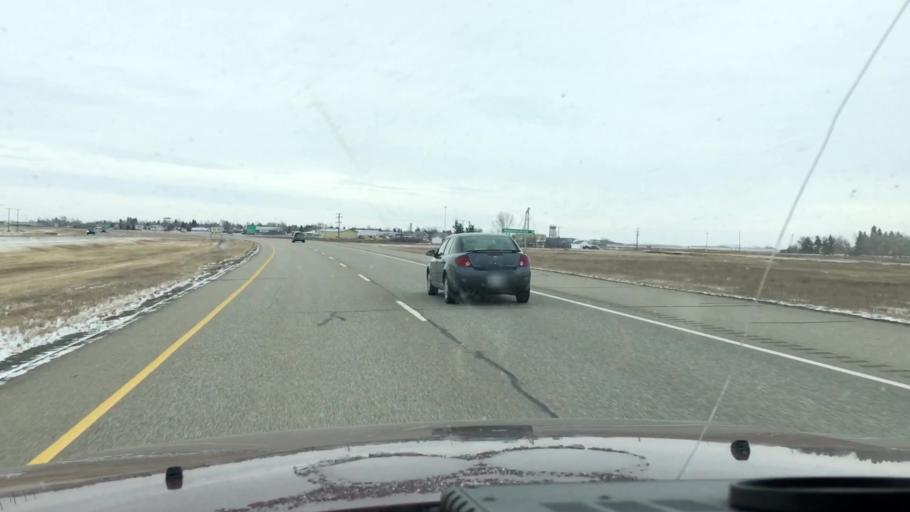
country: CA
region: Saskatchewan
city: Watrous
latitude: 51.2745
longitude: -106.0070
